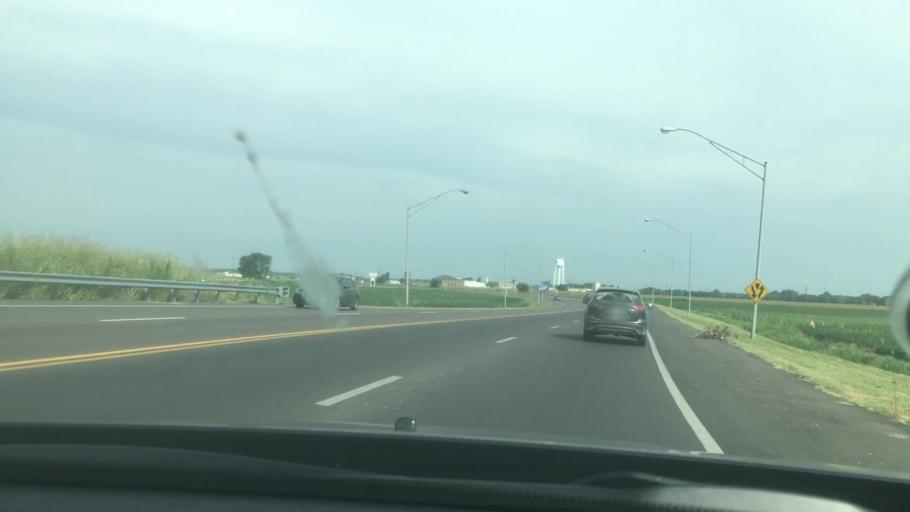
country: US
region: Oklahoma
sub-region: Garvin County
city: Pauls Valley
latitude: 34.7358
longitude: -97.2310
